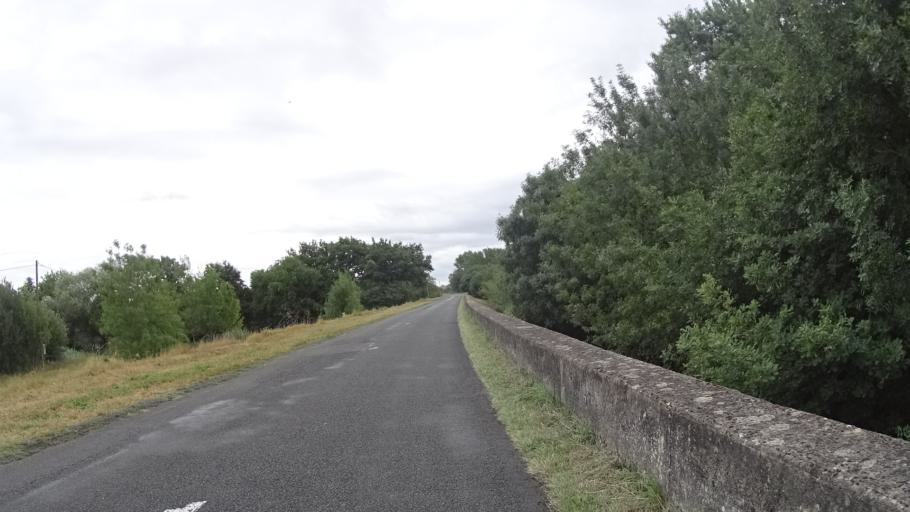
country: FR
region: Pays de la Loire
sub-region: Departement de Maine-et-Loire
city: Chalonnes-sur-Loire
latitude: 47.3666
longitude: -0.7346
